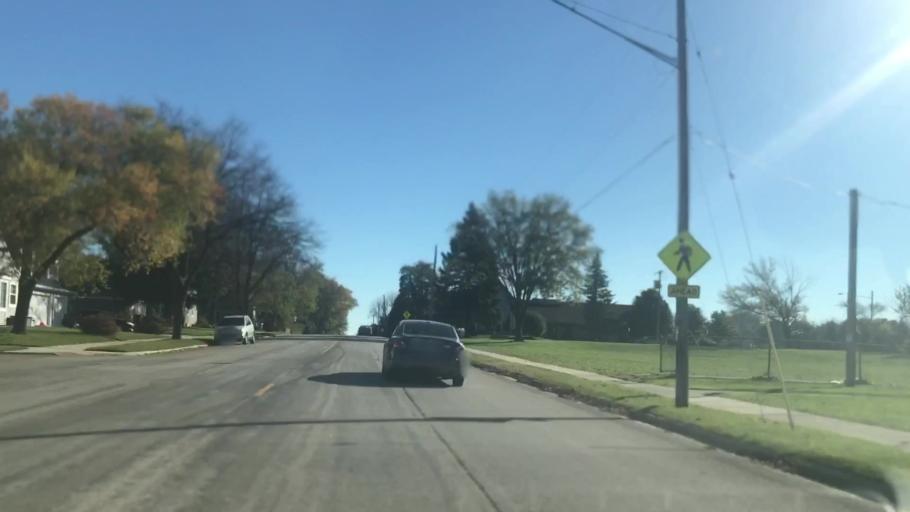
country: US
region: Wisconsin
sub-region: Waukesha County
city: Menomonee Falls
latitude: 43.1703
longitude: -88.1171
